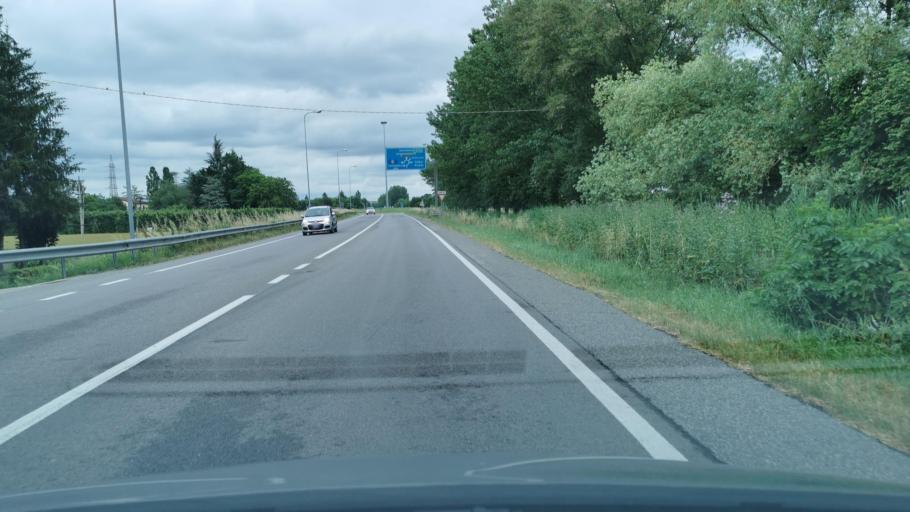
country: IT
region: Emilia-Romagna
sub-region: Provincia di Ravenna
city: Cotignola
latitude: 44.3809
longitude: 11.9504
